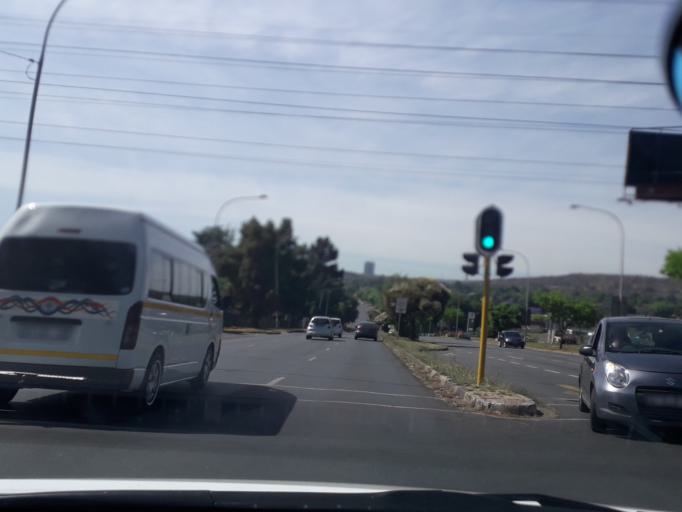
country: ZA
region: Gauteng
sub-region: City of Johannesburg Metropolitan Municipality
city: Johannesburg
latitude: -26.1508
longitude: 27.9884
